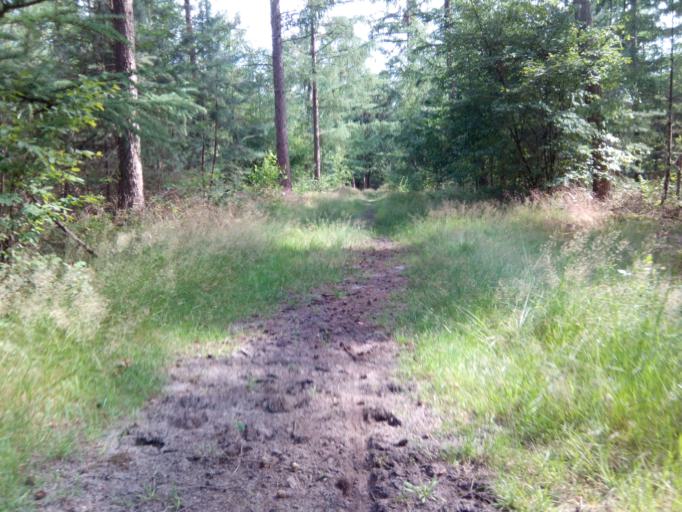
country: NL
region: Utrecht
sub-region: Gemeente Utrechtse Heuvelrug
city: Maarn
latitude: 52.0813
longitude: 5.3612
